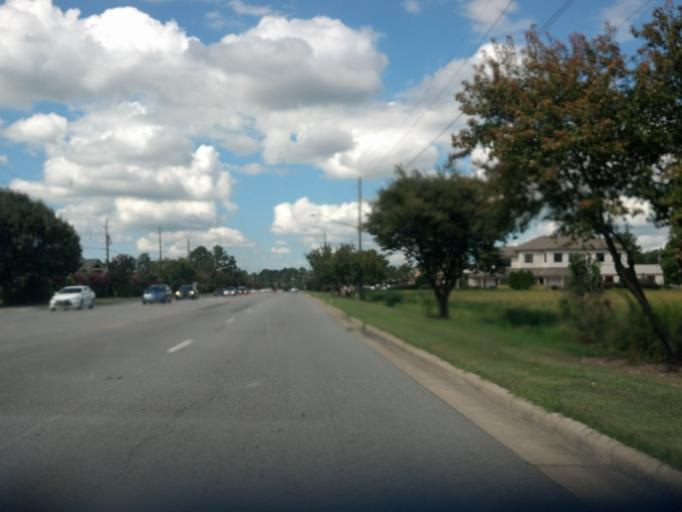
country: US
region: North Carolina
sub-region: Pitt County
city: Windsor
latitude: 35.5745
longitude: -77.3540
